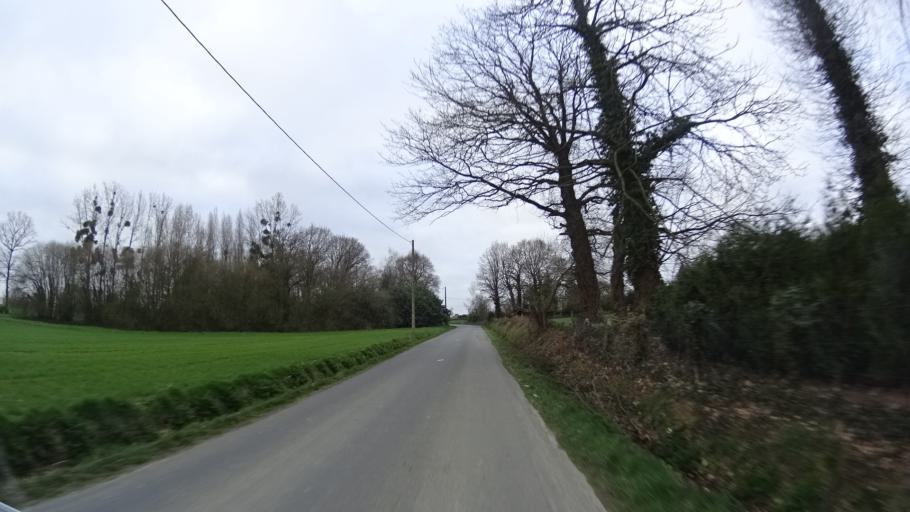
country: FR
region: Brittany
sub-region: Departement d'Ille-et-Vilaine
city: Geveze
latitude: 48.2016
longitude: -1.8302
